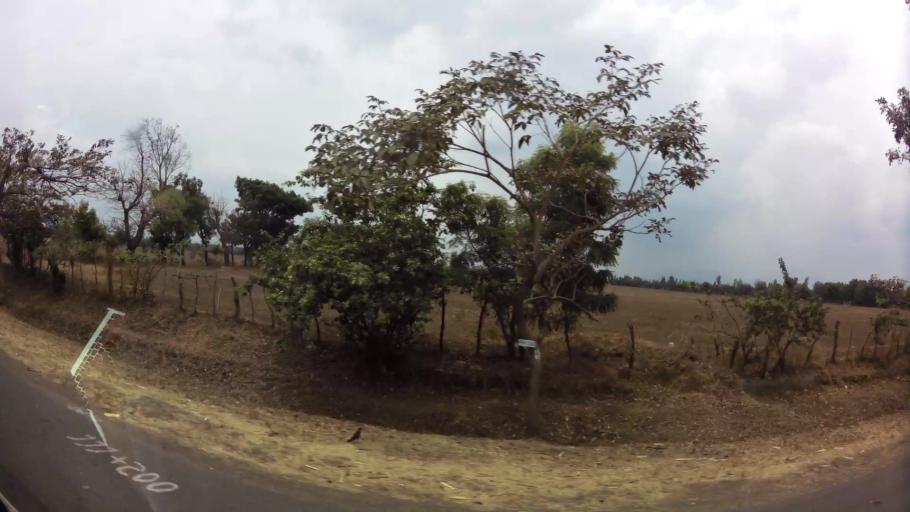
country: NI
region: Chinandega
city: Posoltega
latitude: 12.5565
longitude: -86.9471
